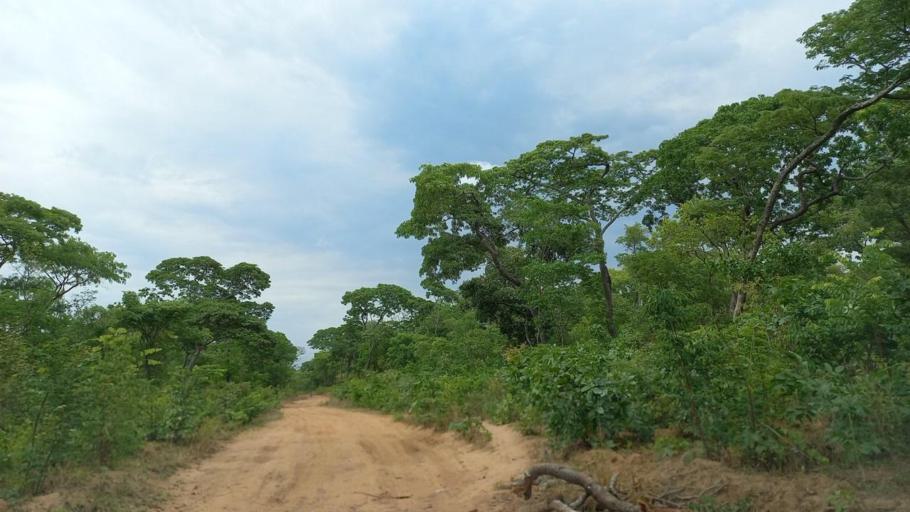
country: ZM
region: North-Western
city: Kalengwa
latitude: -13.5397
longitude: 24.9782
